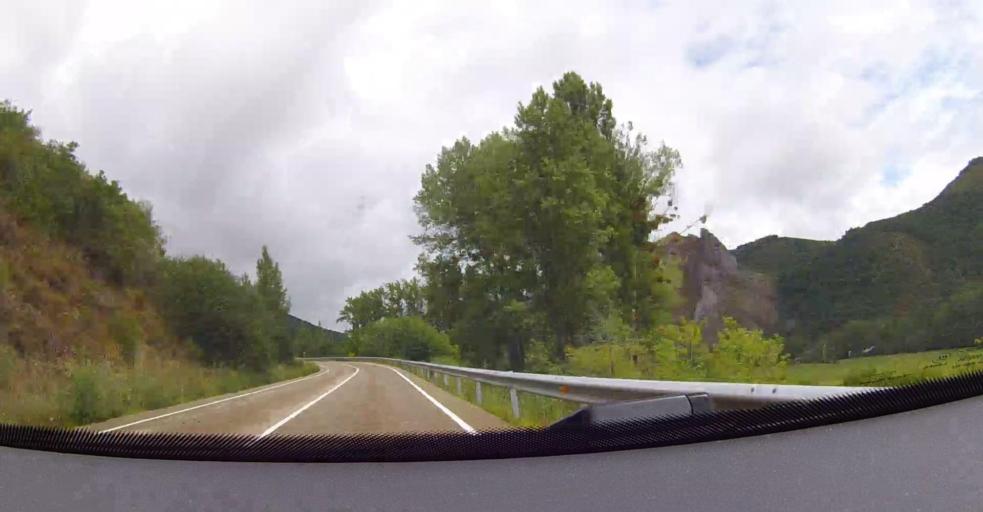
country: ES
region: Castille and Leon
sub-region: Provincia de Leon
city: Bonar
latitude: 42.9019
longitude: -5.3124
